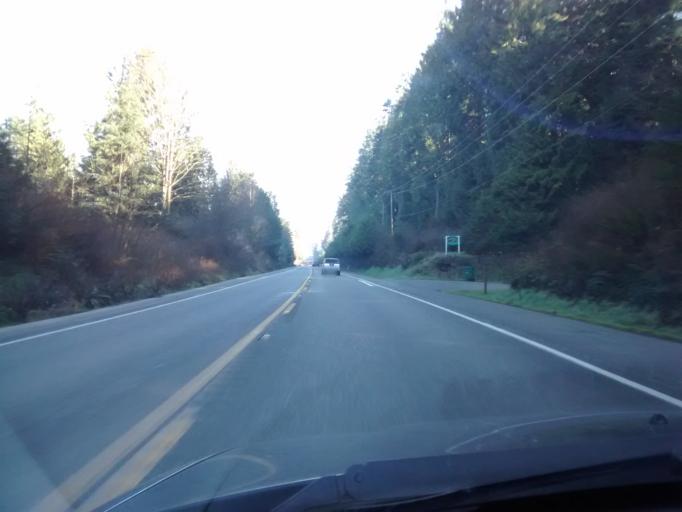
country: US
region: Washington
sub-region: Kitsap County
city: Lofall
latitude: 47.8404
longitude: -122.6171
